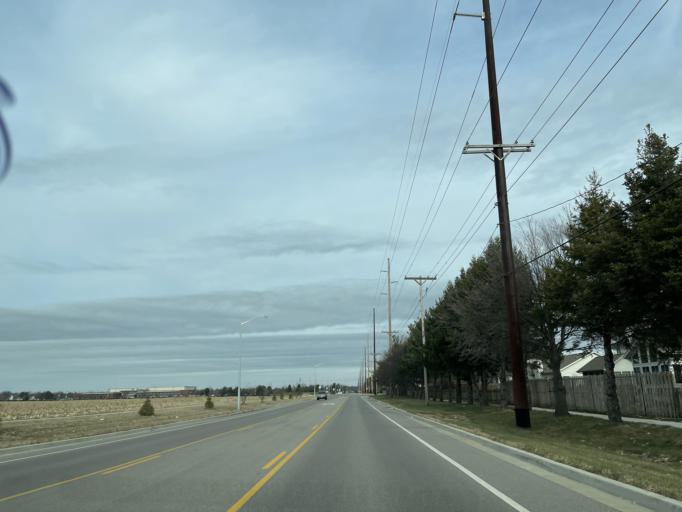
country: US
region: Illinois
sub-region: Sangamon County
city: Jerome
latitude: 39.7652
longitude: -89.7345
